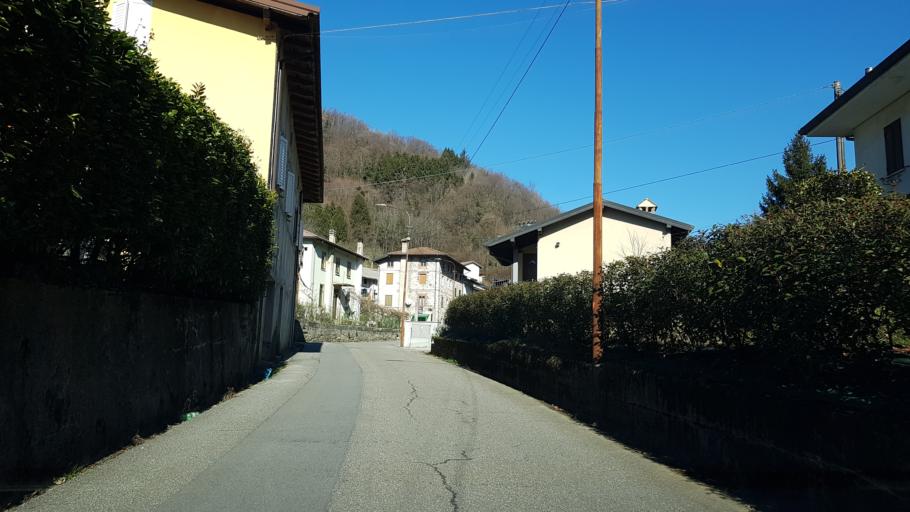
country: IT
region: Friuli Venezia Giulia
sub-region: Provincia di Udine
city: Nimis
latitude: 46.2163
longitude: 13.2939
